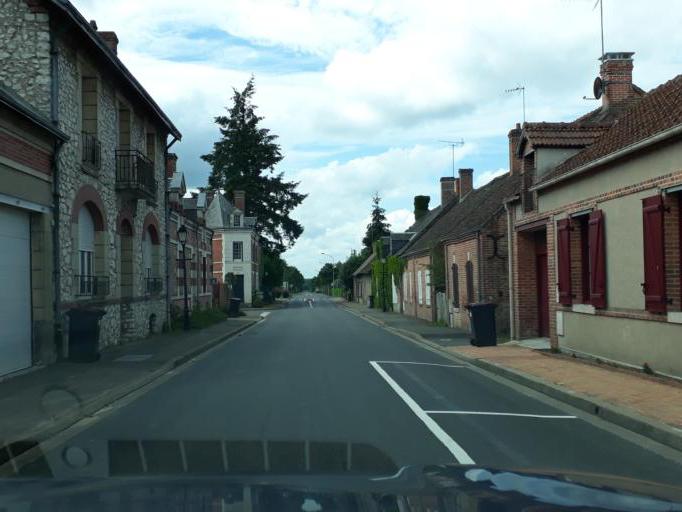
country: FR
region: Centre
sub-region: Departement du Loir-et-Cher
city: Chaumont-sur-Tharonne
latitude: 47.6089
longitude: 1.9037
